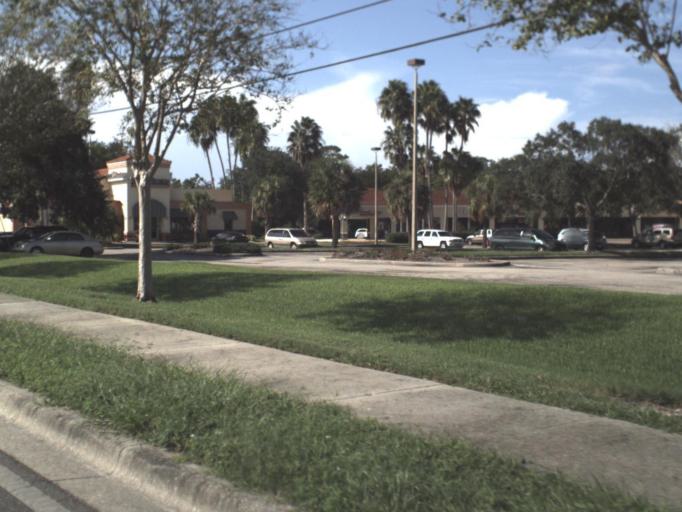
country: US
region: Florida
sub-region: Sarasota County
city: South Sarasota
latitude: 27.2818
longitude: -82.5309
